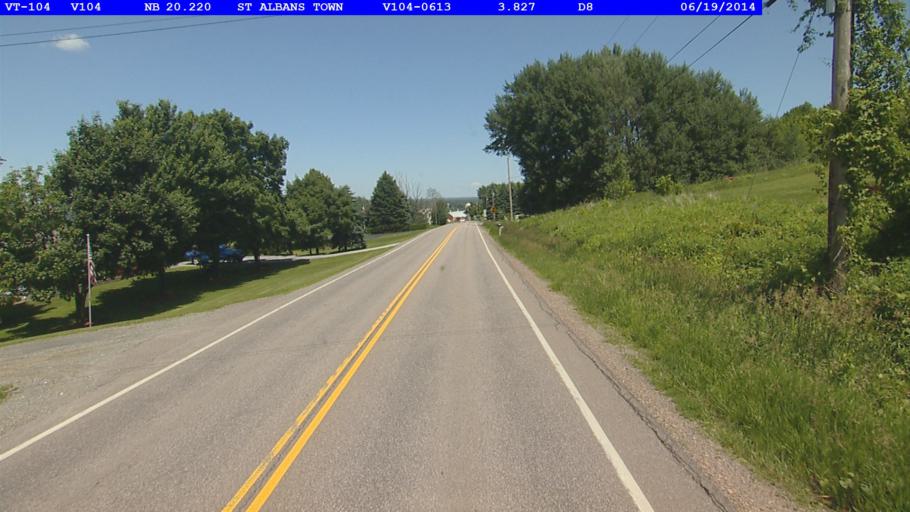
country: US
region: Vermont
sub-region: Franklin County
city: Saint Albans
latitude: 44.8252
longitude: -73.0556
